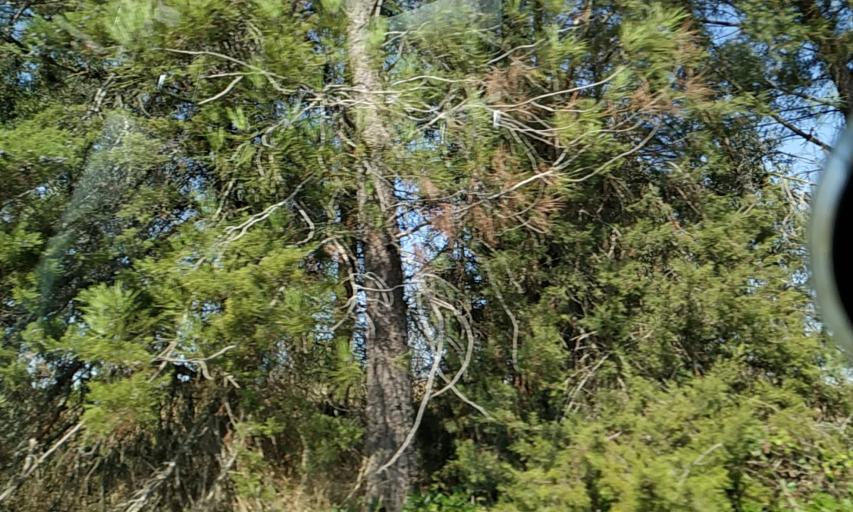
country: PT
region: Santarem
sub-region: Benavente
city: Poceirao
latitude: 38.7524
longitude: -8.6317
